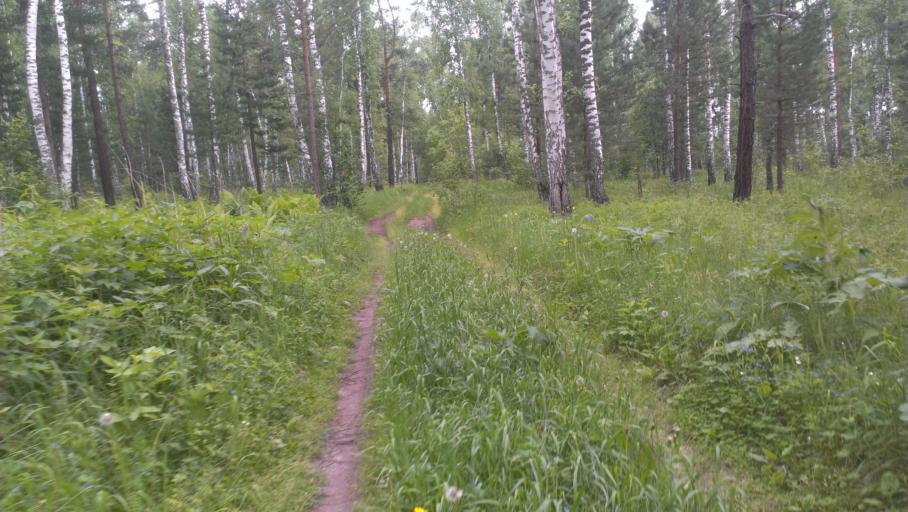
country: RU
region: Altai Krai
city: Sannikovo
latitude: 53.3395
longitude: 84.0492
